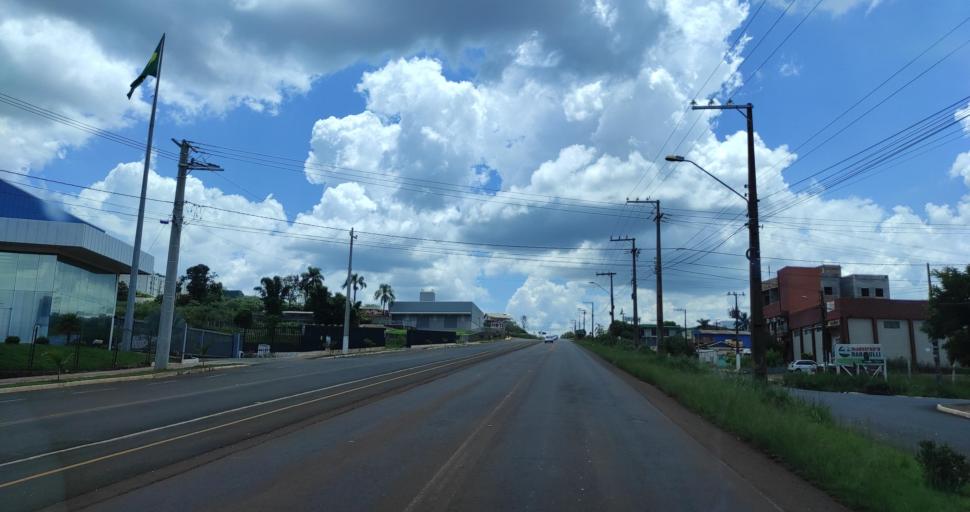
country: BR
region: Santa Catarina
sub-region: Xanxere
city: Xanxere
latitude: -26.8598
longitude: -52.4058
